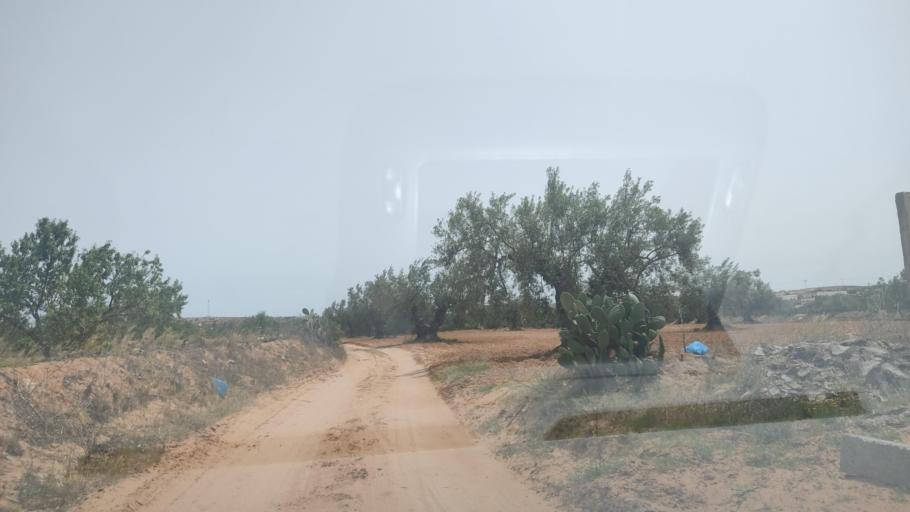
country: TN
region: Safaqis
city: Sfax
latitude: 34.8349
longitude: 10.5992
